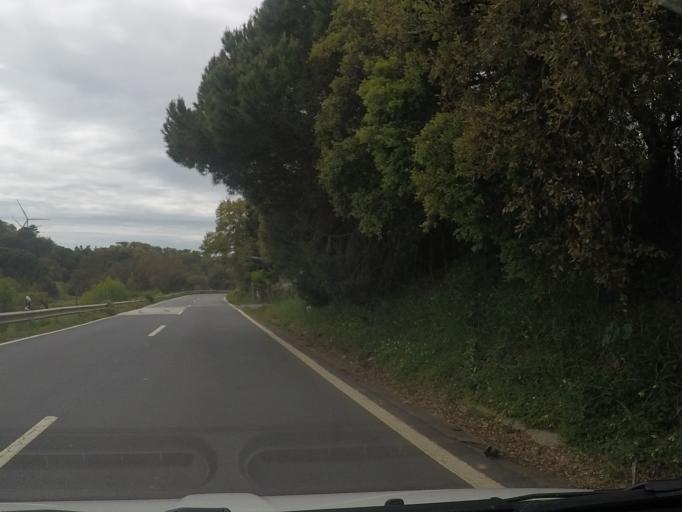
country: PT
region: Setubal
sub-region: Sines
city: Porto Covo
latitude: 37.8682
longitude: -8.7375
